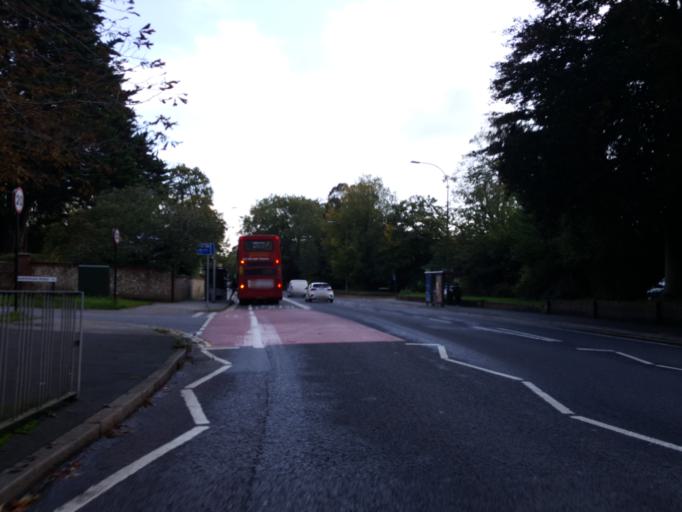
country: GB
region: England
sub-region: Brighton and Hove
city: Hove
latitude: 50.8488
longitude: -0.1527
